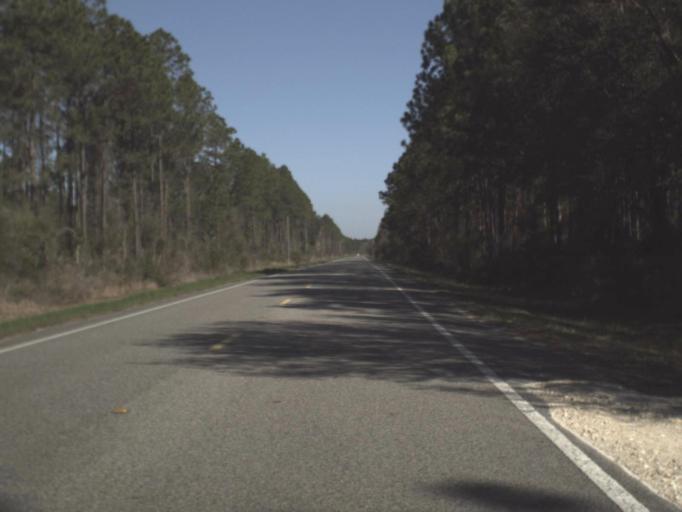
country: US
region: Florida
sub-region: Leon County
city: Woodville
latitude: 30.2972
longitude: -84.0480
